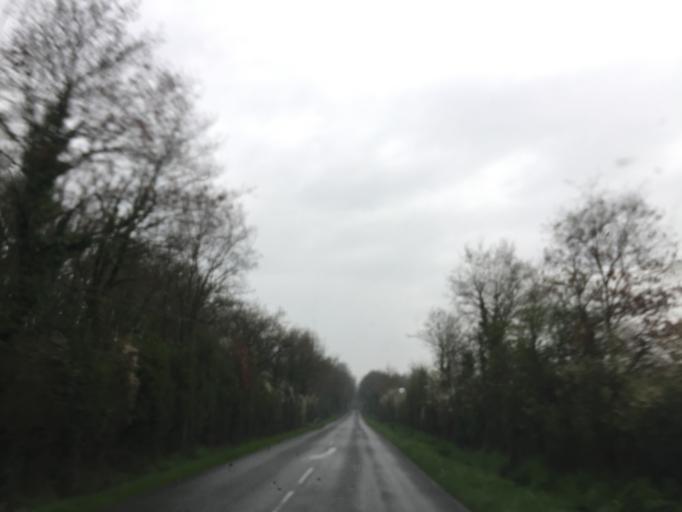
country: FR
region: Pays de la Loire
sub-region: Departement de la Loire-Atlantique
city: Casson
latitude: 47.3756
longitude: -1.5211
